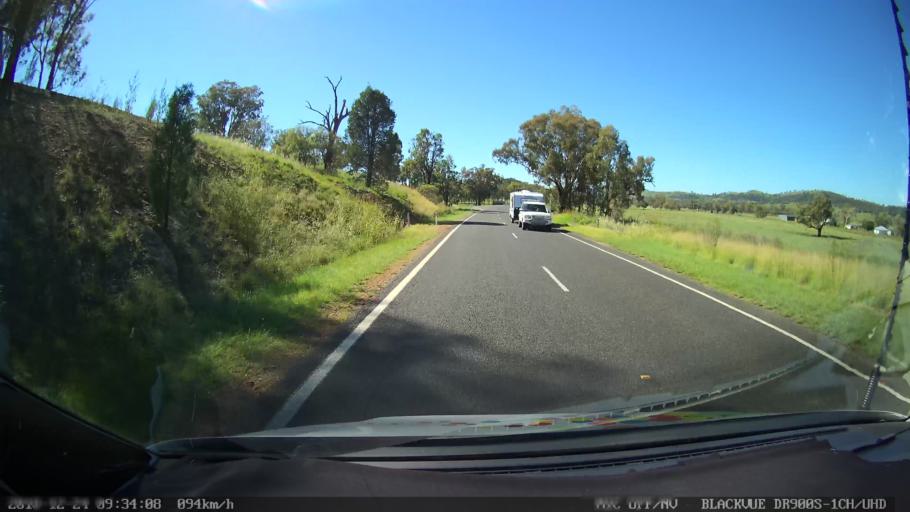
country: AU
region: New South Wales
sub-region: Liverpool Plains
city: Quirindi
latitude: -31.6109
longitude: 150.7138
